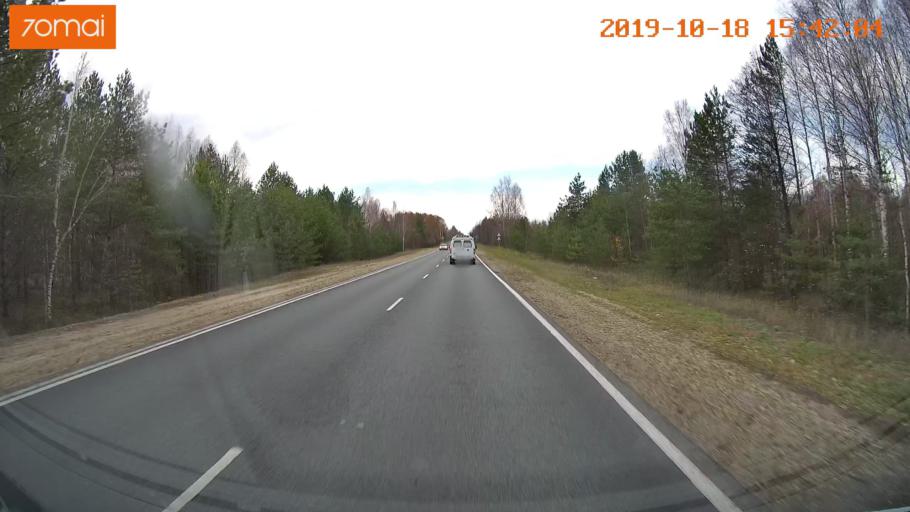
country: RU
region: Vladimir
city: Golovino
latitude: 55.9518
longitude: 40.5735
